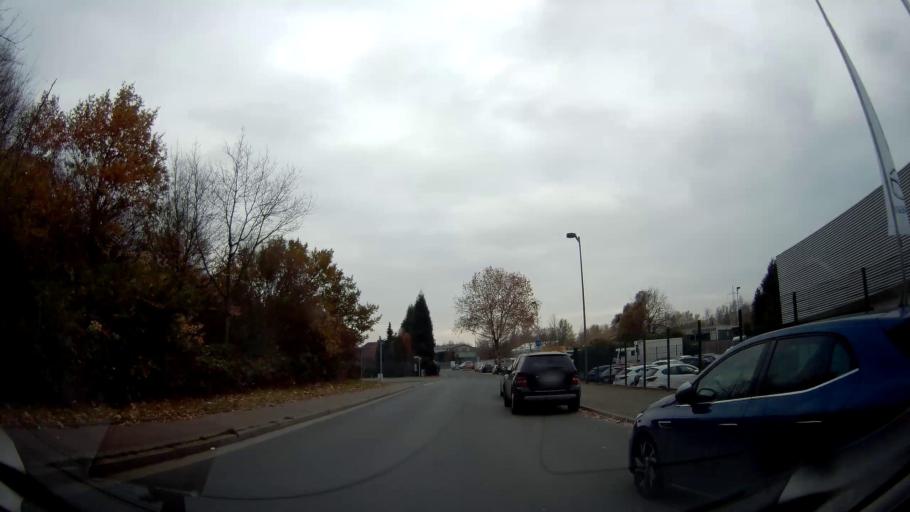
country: DE
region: North Rhine-Westphalia
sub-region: Regierungsbezirk Munster
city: Gladbeck
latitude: 51.5521
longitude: 7.0378
